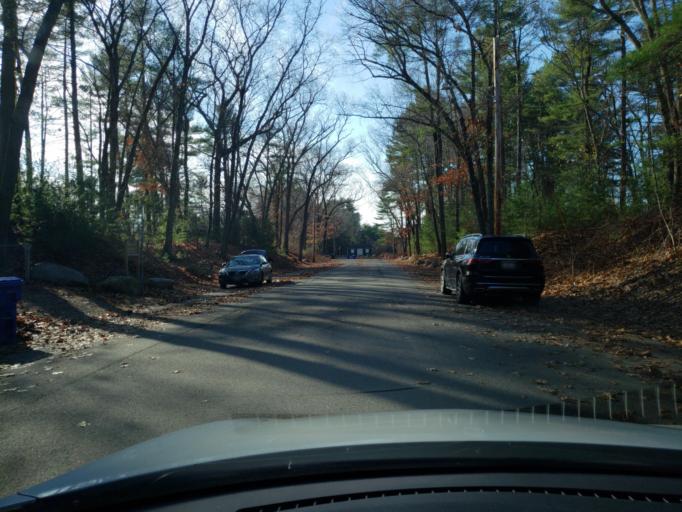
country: US
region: Massachusetts
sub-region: Essex County
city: Andover
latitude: 42.6330
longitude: -71.1478
